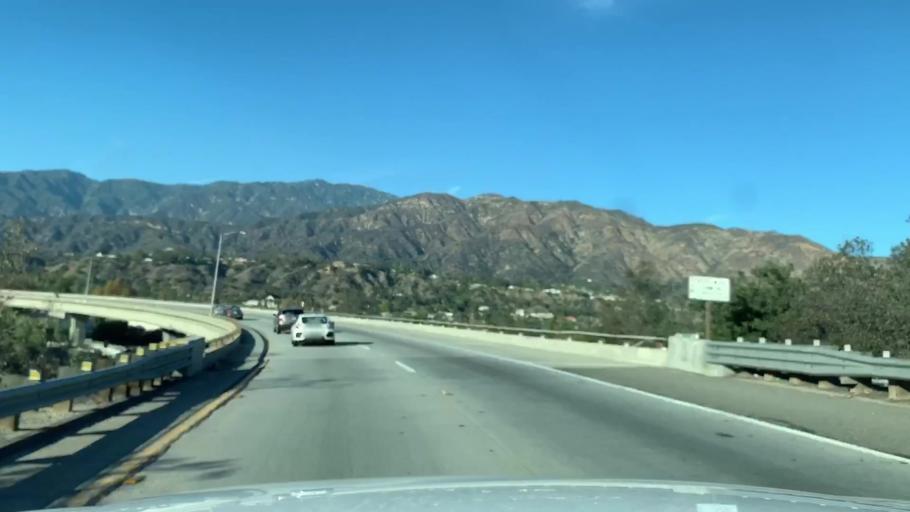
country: US
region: California
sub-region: Los Angeles County
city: Bradbury
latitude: 34.1334
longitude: -117.9589
